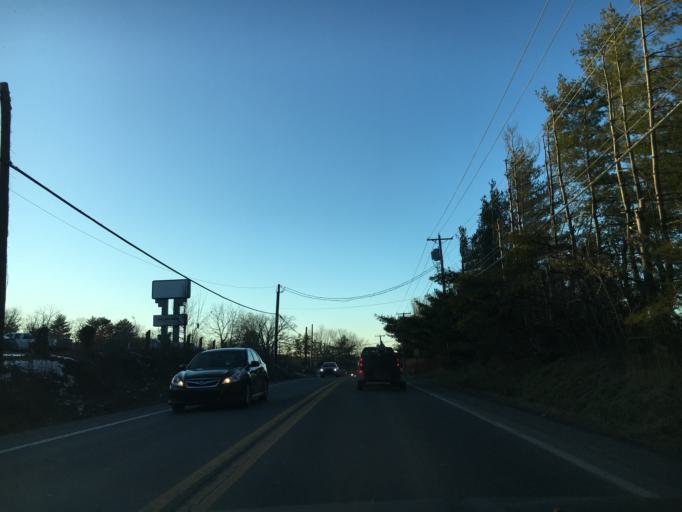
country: US
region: West Virginia
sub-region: Raleigh County
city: Daniels
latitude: 37.7415
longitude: -81.1187
